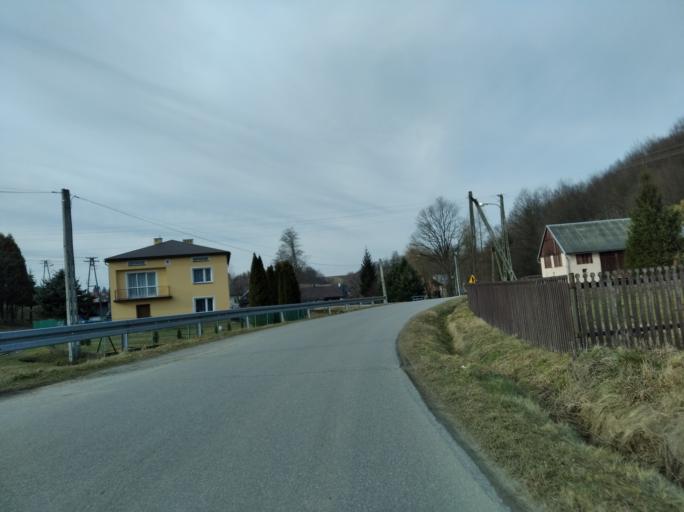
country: PL
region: Subcarpathian Voivodeship
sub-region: Powiat brzozowski
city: Gorki
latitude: 49.6422
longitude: 22.0519
